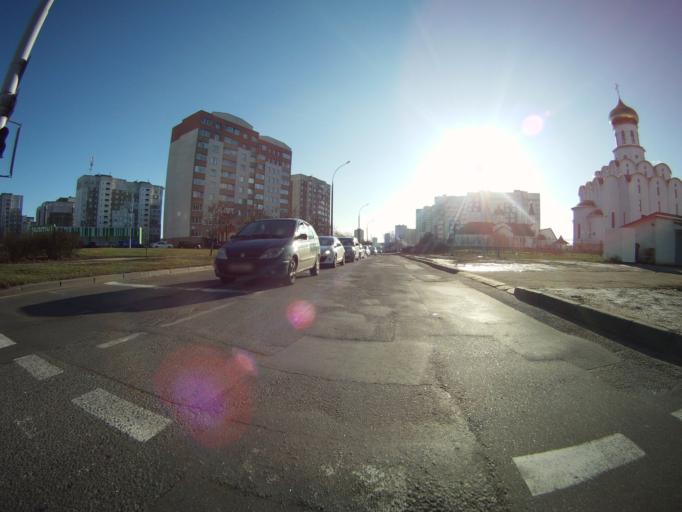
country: BY
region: Minsk
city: Novoye Medvezhino
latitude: 53.8818
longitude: 27.4395
